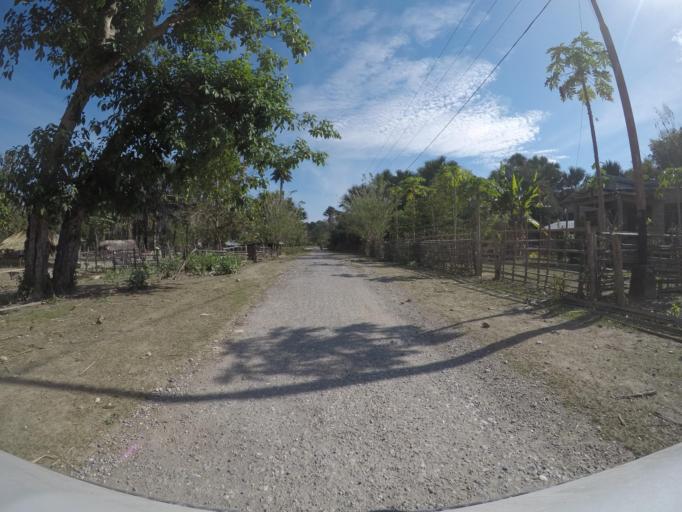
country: TL
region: Bobonaro
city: Maliana
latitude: -8.8459
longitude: 125.2186
